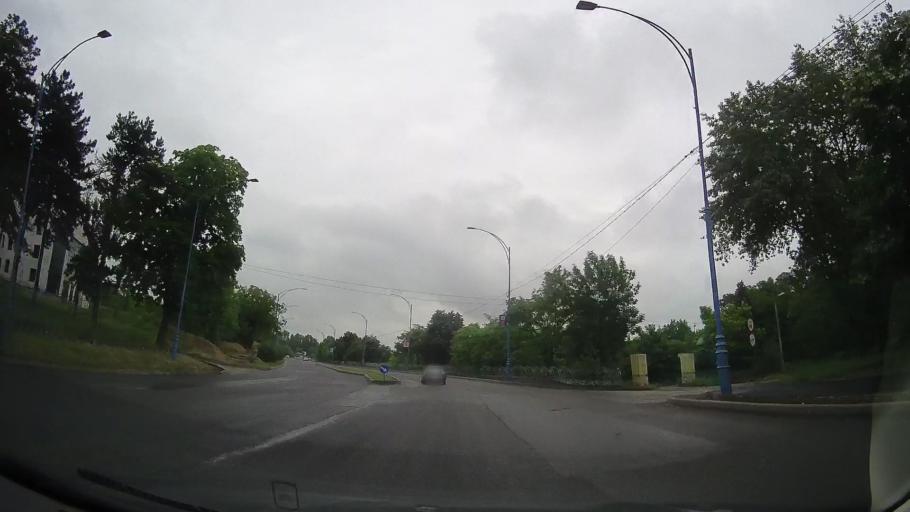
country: RO
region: Mehedinti
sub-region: Municipiul Drobeta-Turnu Severin
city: Drobeta-Turnu Severin
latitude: 44.6257
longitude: 22.6392
